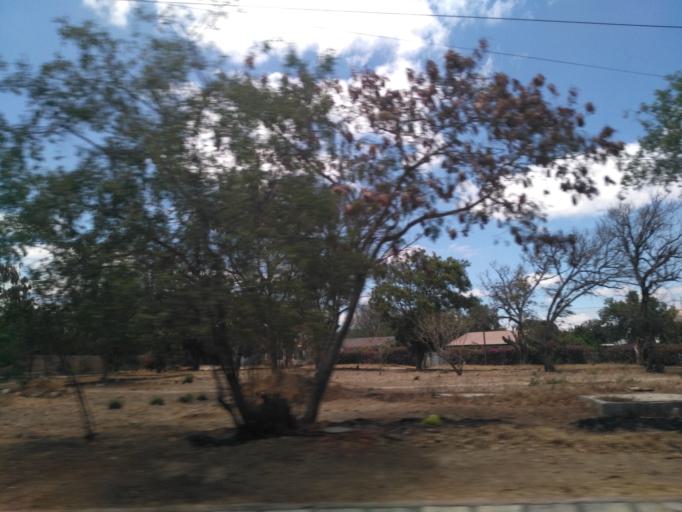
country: TZ
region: Dodoma
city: Dodoma
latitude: -6.1866
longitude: 35.7445
